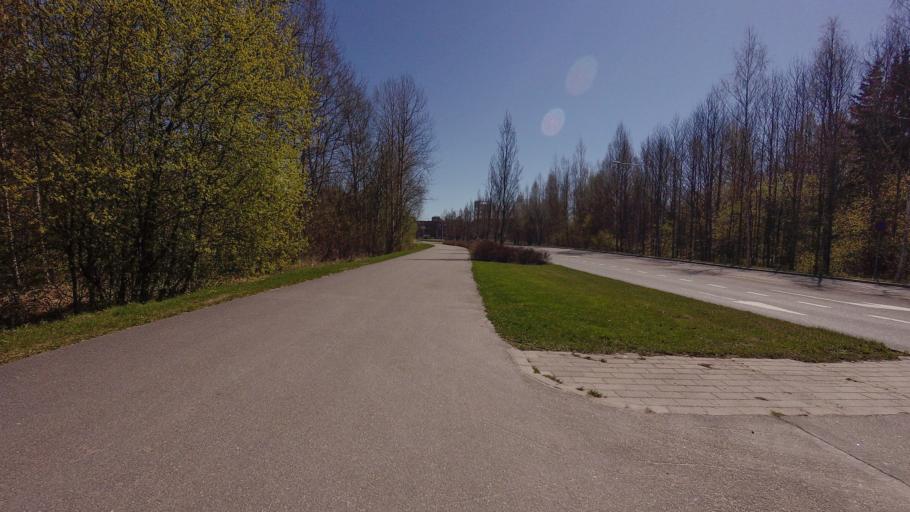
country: FI
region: Uusimaa
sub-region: Helsinki
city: Vantaa
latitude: 60.2301
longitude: 25.1211
